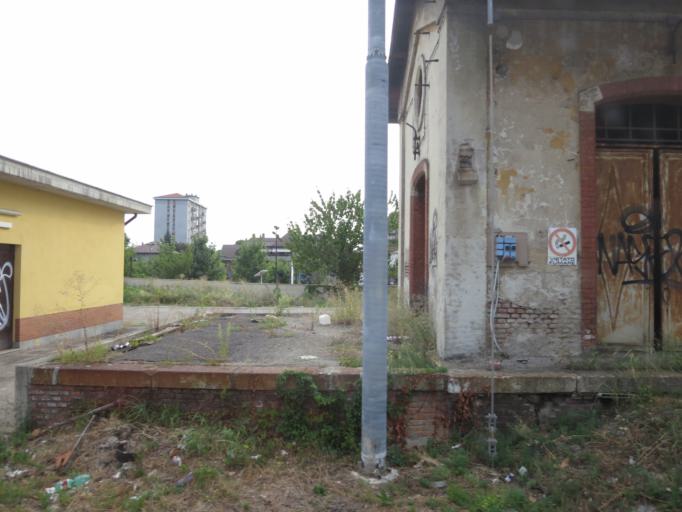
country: IT
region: Lombardy
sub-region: Provincia di Monza e Brianza
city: Desio
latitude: 45.6209
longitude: 9.2181
